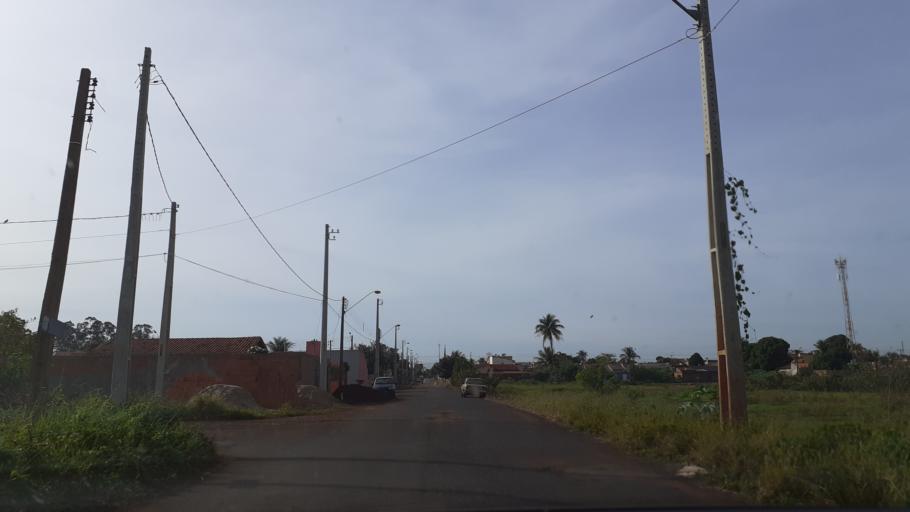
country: BR
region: Goias
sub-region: Itumbiara
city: Itumbiara
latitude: -18.4148
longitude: -49.2478
